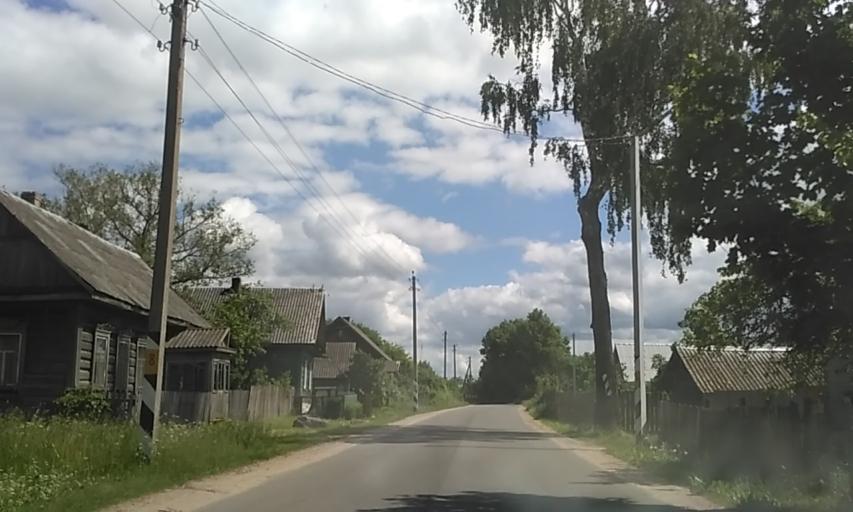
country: BY
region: Minsk
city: Krupki
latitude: 54.3524
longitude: 29.1147
